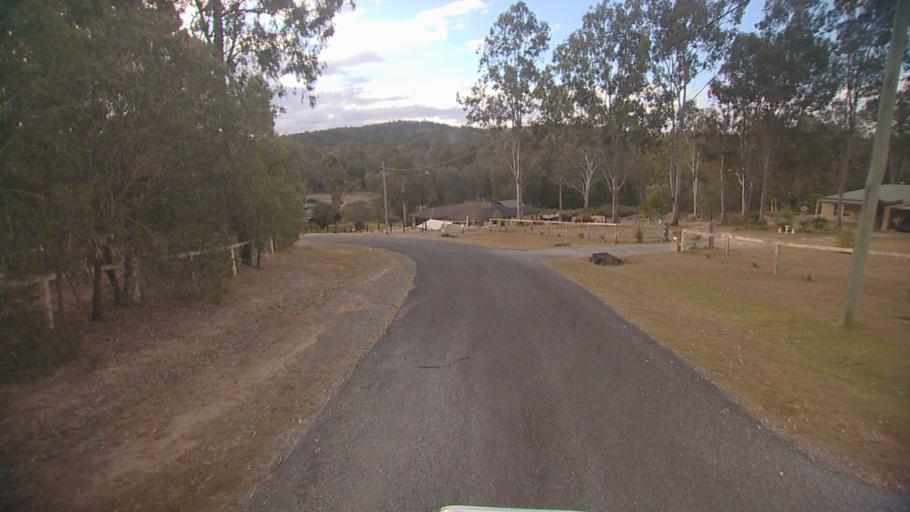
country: AU
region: Queensland
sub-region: Logan
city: Cedar Vale
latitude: -27.9324
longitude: 153.0667
